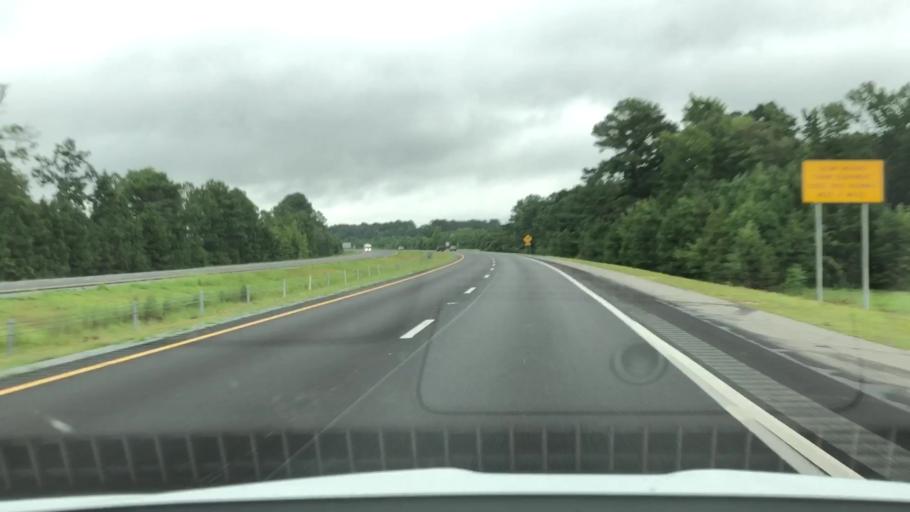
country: US
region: North Carolina
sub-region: Wayne County
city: Goldsboro
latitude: 35.4327
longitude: -77.9869
